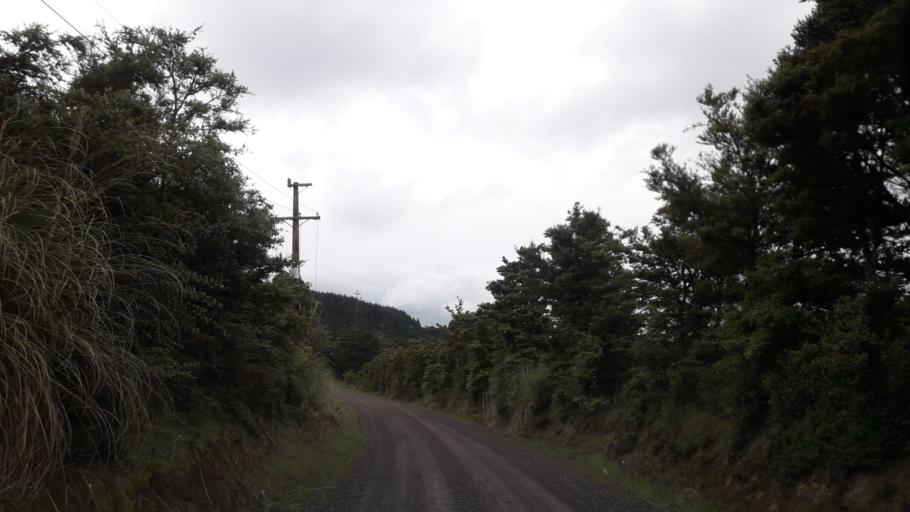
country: NZ
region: Northland
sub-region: Far North District
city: Kaitaia
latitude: -35.3787
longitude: 173.4107
